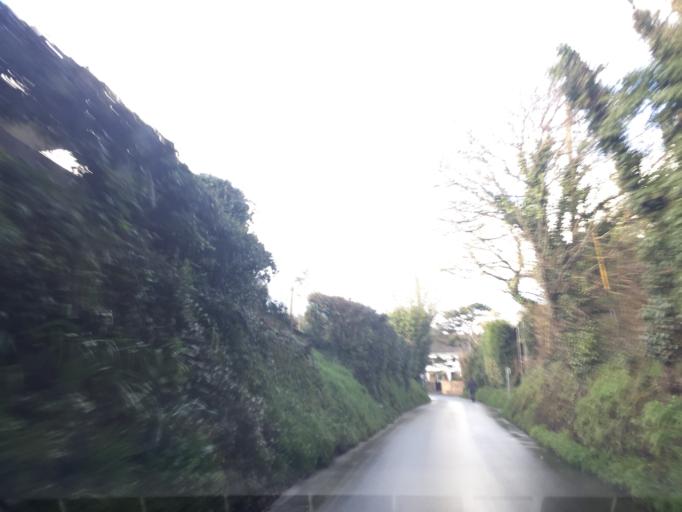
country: JE
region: St Helier
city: Saint Helier
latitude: 49.2034
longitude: -2.1376
